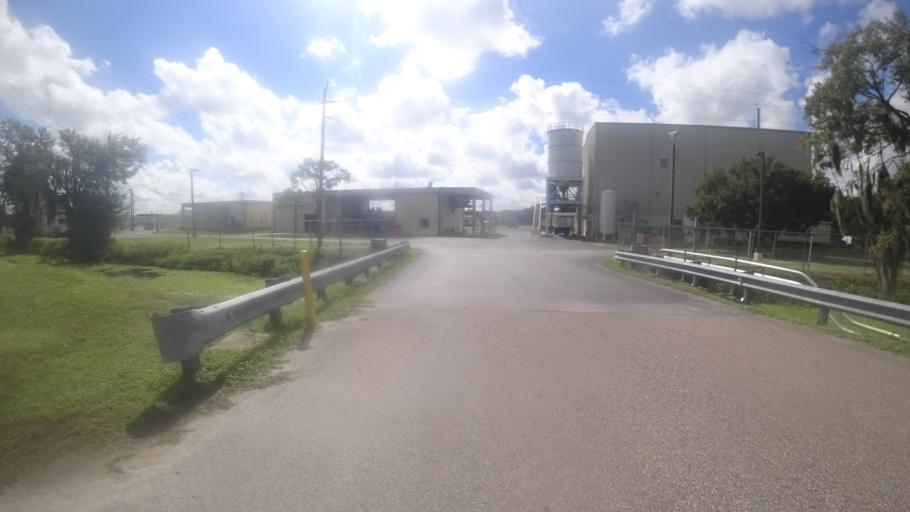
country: US
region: Florida
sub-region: Manatee County
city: Samoset
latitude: 27.4690
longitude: -82.4517
